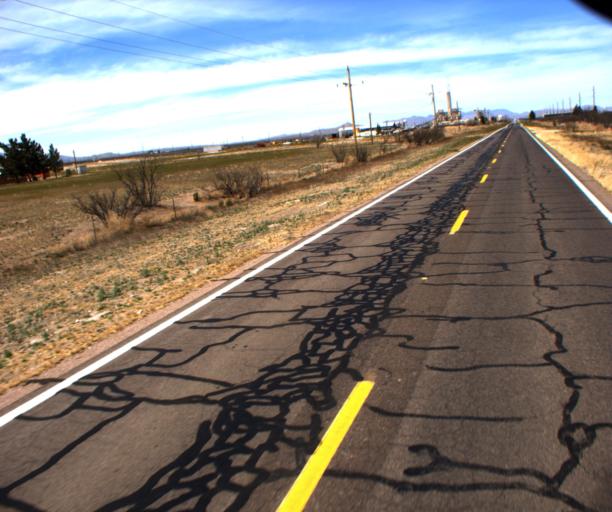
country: US
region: Arizona
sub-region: Cochise County
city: Willcox
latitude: 32.0435
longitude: -109.8827
